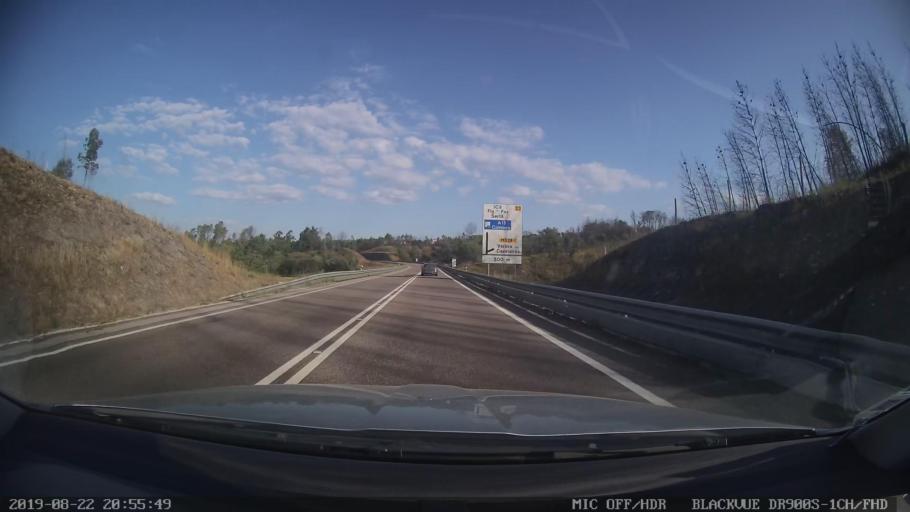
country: PT
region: Castelo Branco
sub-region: Serta
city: Serta
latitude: 39.7839
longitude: -8.0399
